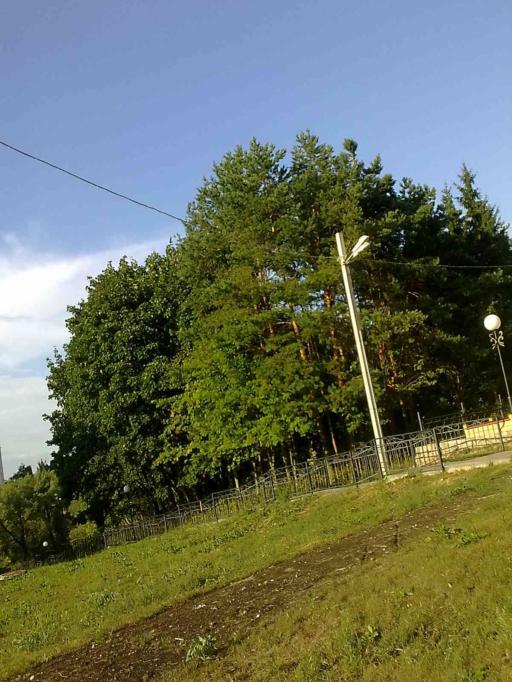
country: RU
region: Moskovskaya
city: Kommunarka
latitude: 55.5275
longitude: 37.4397
